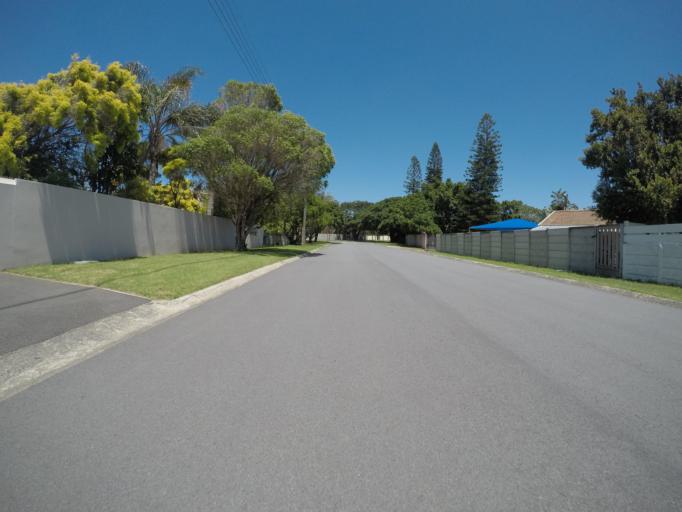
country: ZA
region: Eastern Cape
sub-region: Buffalo City Metropolitan Municipality
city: East London
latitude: -32.9656
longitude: 27.9466
